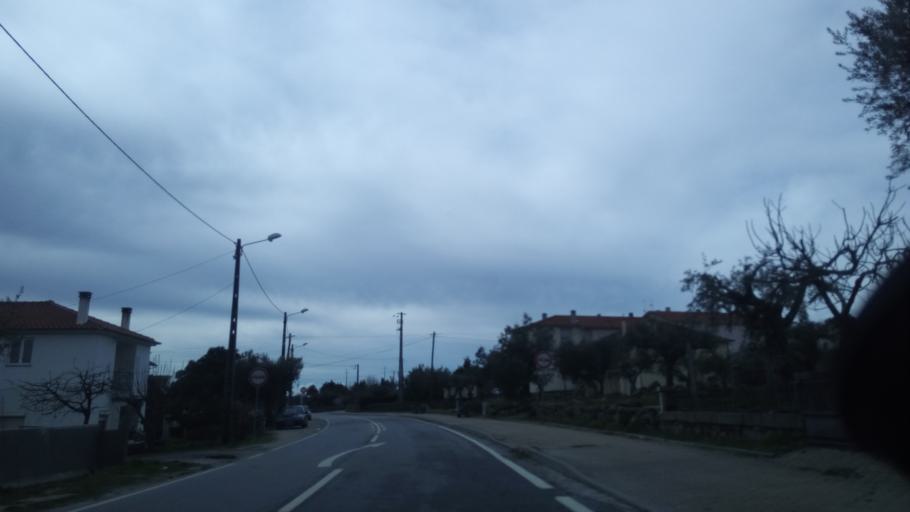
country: PT
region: Guarda
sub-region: Seia
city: Seia
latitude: 40.4644
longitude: -7.6866
